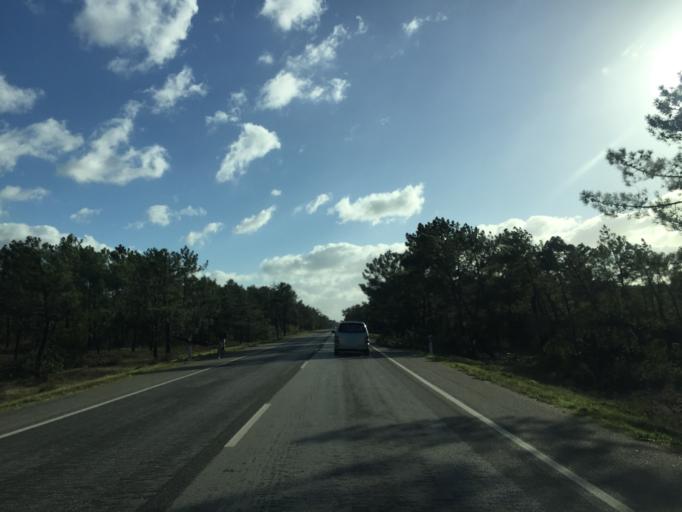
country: PT
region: Coimbra
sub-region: Figueira da Foz
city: Lavos
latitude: 40.0707
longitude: -8.8650
